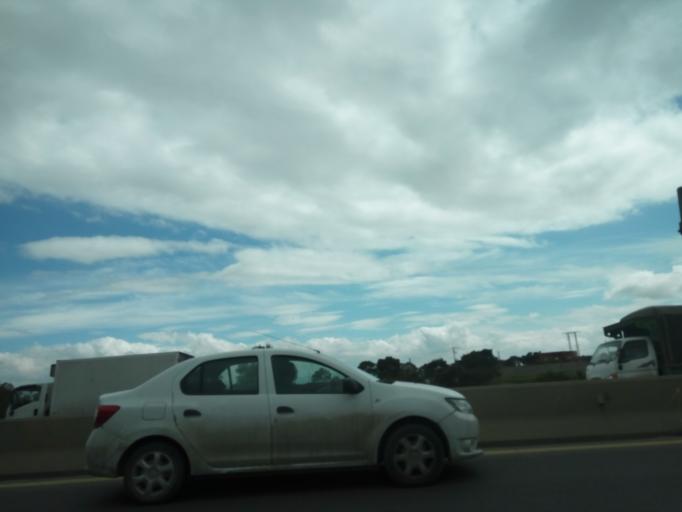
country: DZ
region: Bordj Bou Arreridj
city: Bordj Bou Arreridj
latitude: 36.0961
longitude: 4.7593
